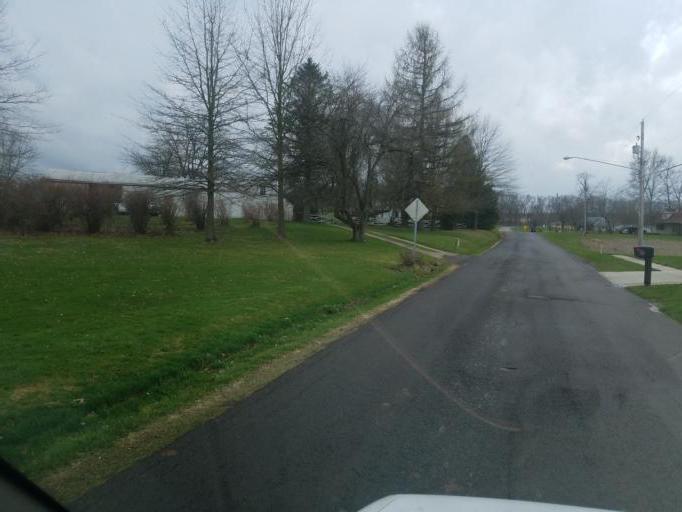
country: US
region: Ohio
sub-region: Sandusky County
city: Bellville
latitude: 40.6139
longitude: -82.5217
